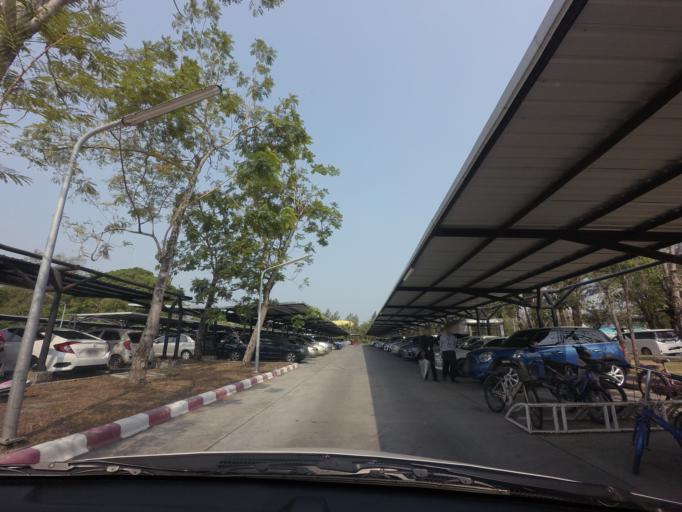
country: TH
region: Nakhon Pathom
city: Salaya
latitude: 13.7920
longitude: 100.3181
